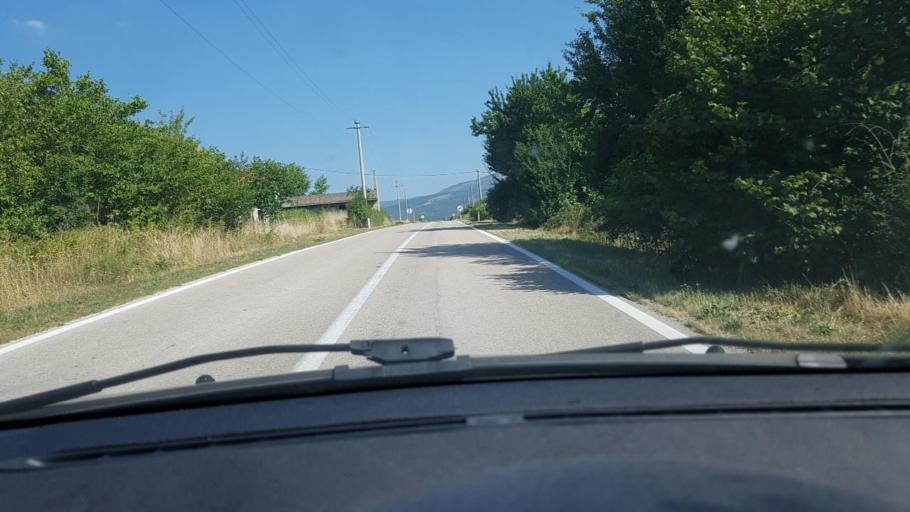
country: BA
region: Federation of Bosnia and Herzegovina
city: Bosansko Grahovo
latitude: 44.0561
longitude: 16.5848
